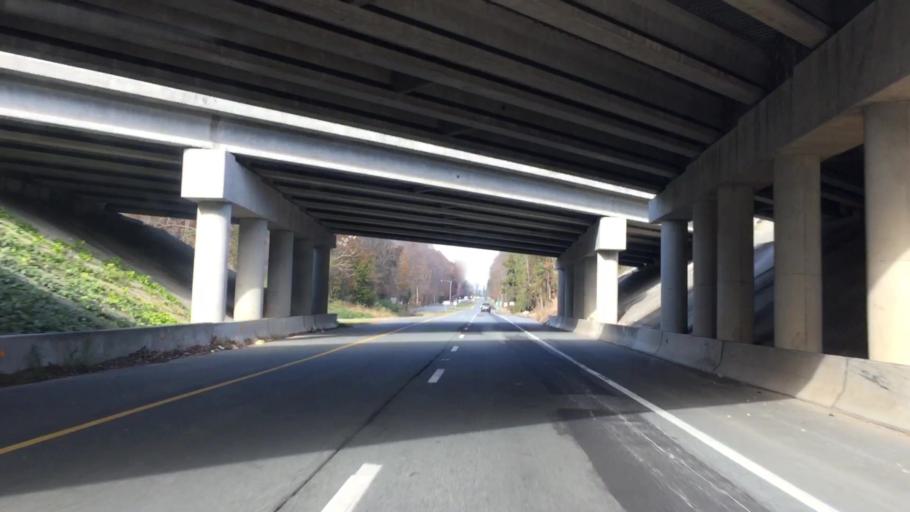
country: US
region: North Carolina
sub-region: Forsyth County
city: Winston-Salem
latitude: 36.1016
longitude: -80.1936
